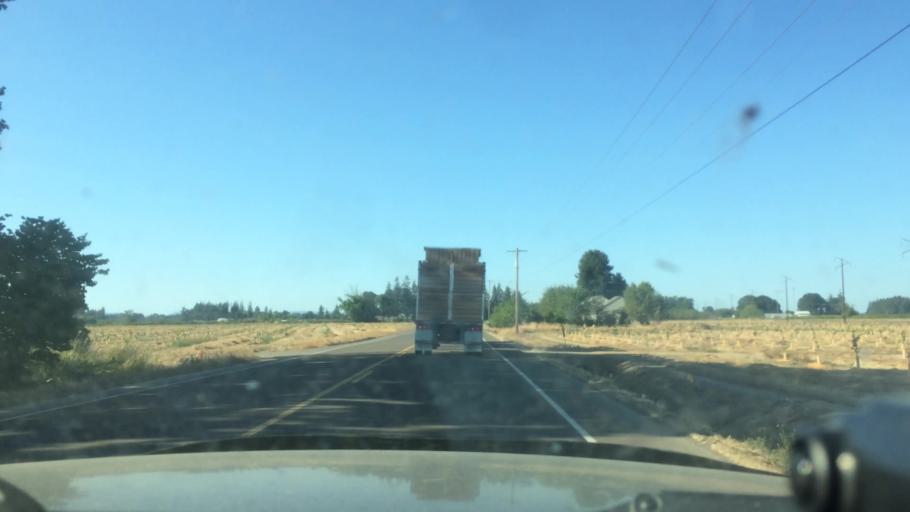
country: US
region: Oregon
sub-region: Marion County
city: Hayesville
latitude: 45.0639
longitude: -122.9809
